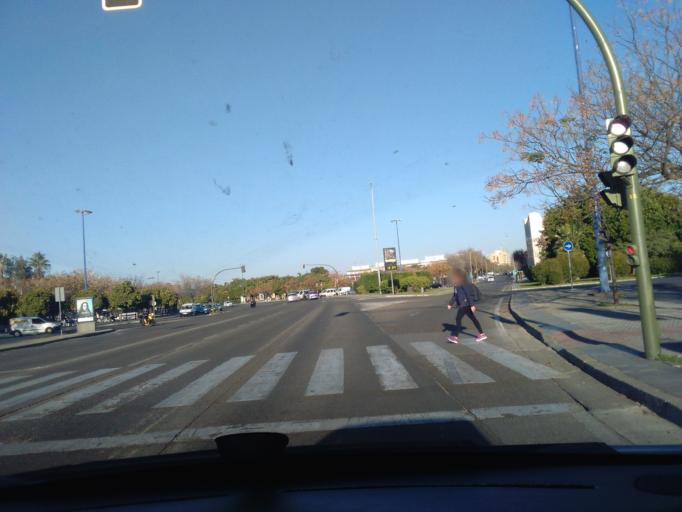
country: ES
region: Andalusia
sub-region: Provincia de Sevilla
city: Sevilla
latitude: 37.3763
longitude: -5.9615
